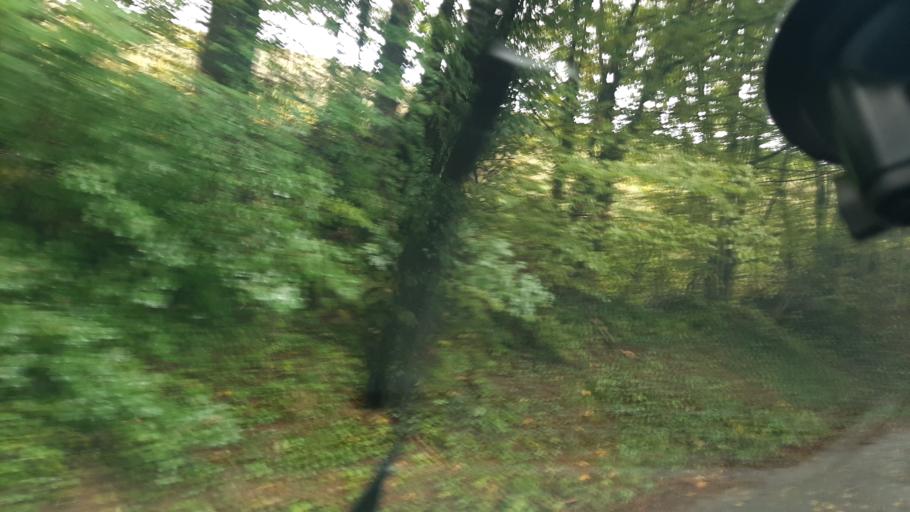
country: FR
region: Rhone-Alpes
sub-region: Departement de la Savoie
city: Gresy-sur-Isere
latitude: 45.6273
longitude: 6.2785
